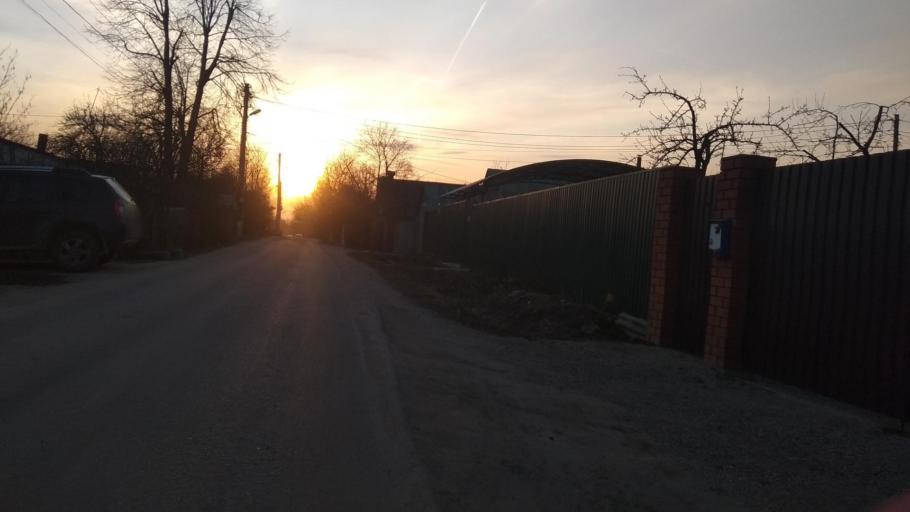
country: RU
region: Moskovskaya
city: Vidnoye
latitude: 55.5610
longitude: 37.6954
